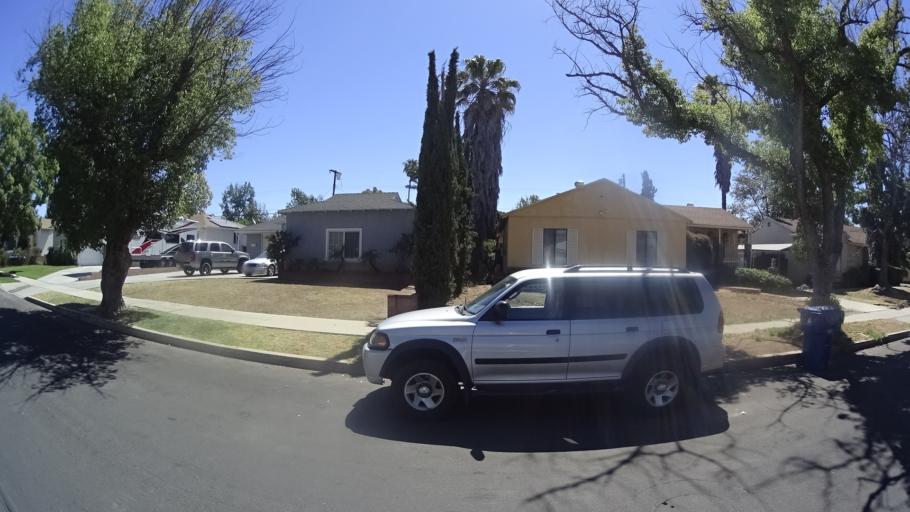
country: US
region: California
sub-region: Los Angeles County
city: San Fernando
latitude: 34.2530
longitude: -118.4631
